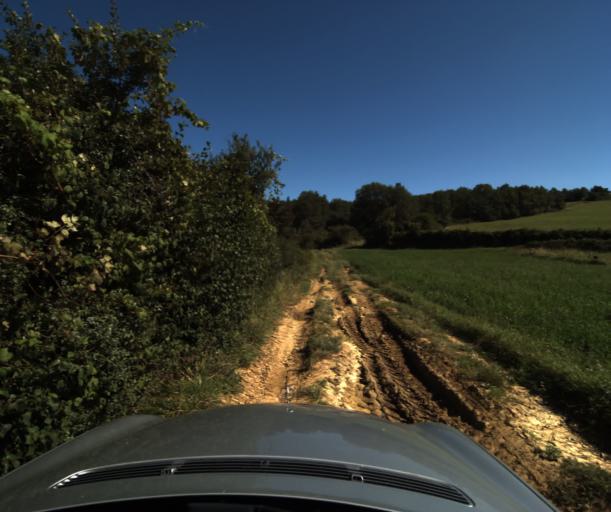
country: FR
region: Midi-Pyrenees
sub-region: Departement de l'Ariege
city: Belesta
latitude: 42.9722
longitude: 1.9192
